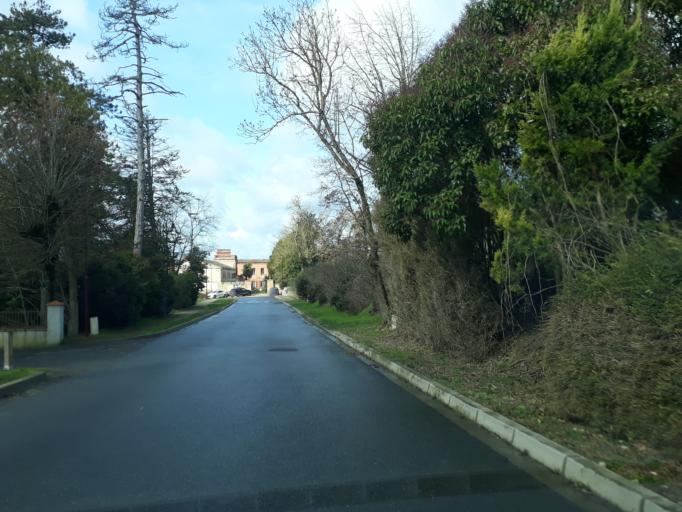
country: FR
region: Midi-Pyrenees
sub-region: Departement du Gers
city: Gimont
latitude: 43.6405
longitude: 0.9994
